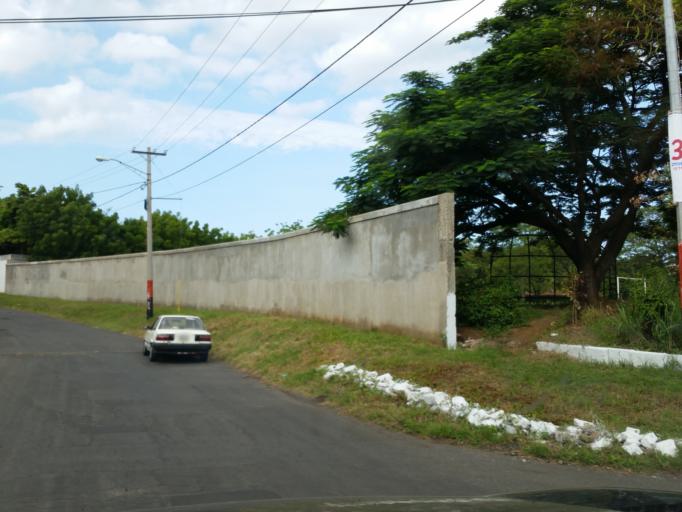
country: NI
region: Managua
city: Managua
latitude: 12.0937
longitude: -86.2411
